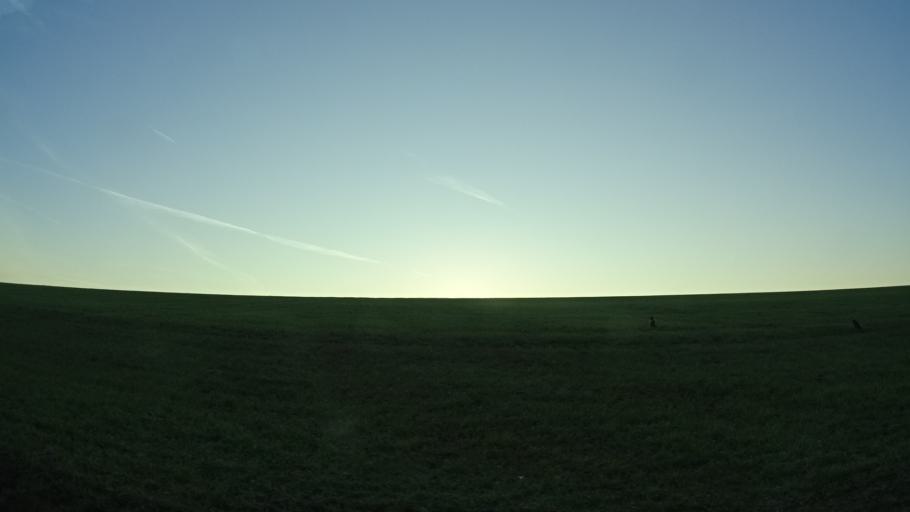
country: DE
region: Saarland
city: Sankt Wendel
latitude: 49.5063
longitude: 7.2063
